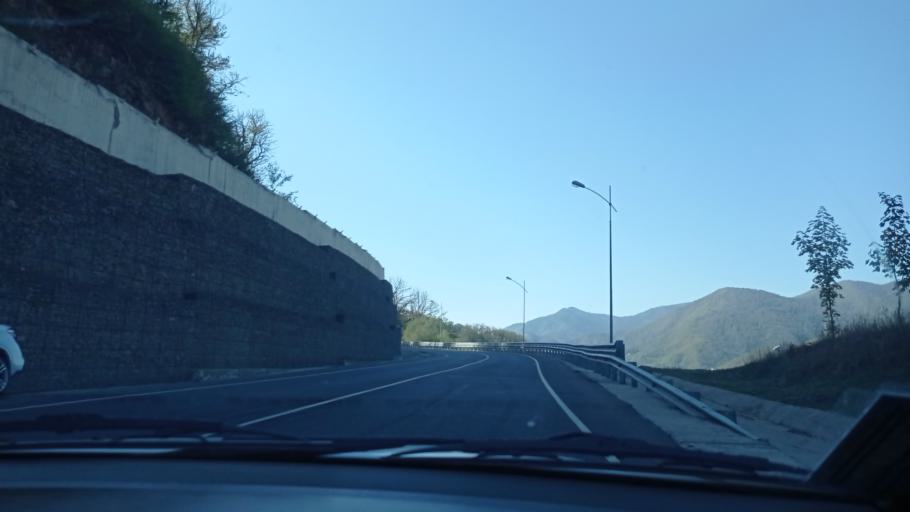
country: RU
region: Krasnodarskiy
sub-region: Sochi City
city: Krasnaya Polyana
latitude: 43.6816
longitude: 40.2460
